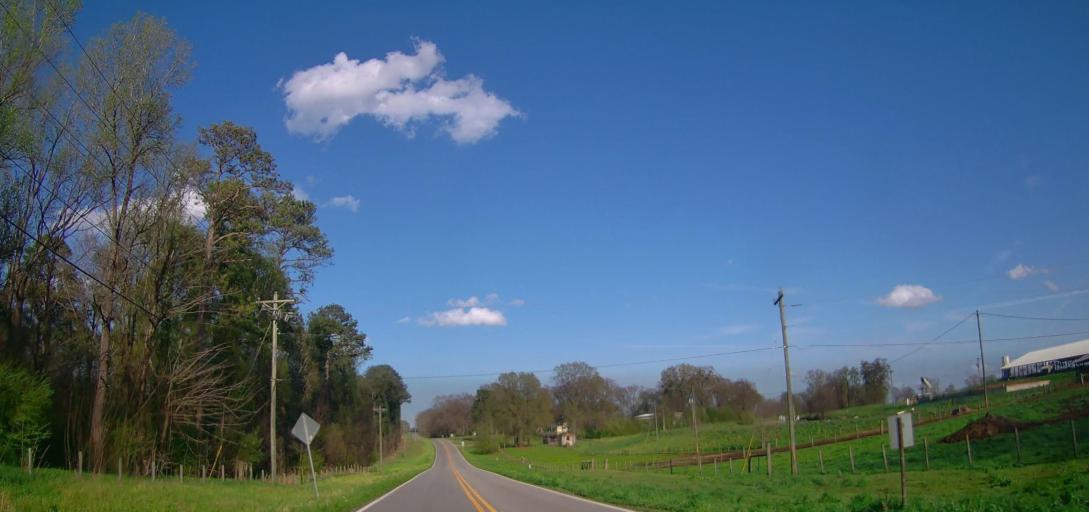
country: US
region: Georgia
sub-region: Putnam County
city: Eatonton
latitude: 33.1965
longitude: -83.4187
